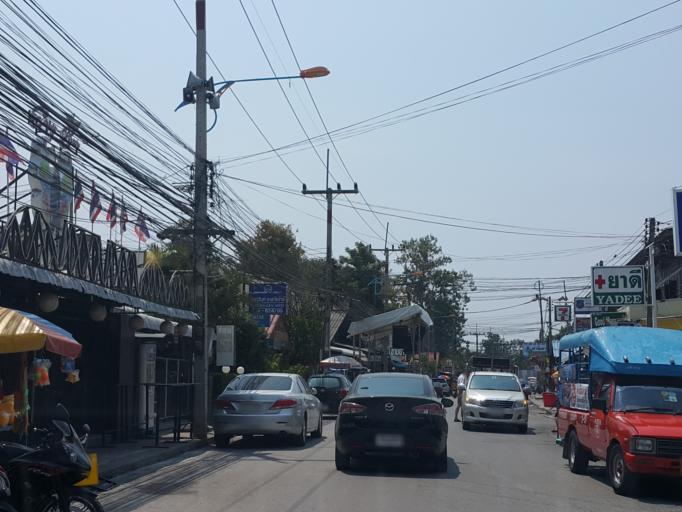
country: TH
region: Kanchanaburi
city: Kanchanaburi
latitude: 14.0337
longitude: 99.5202
